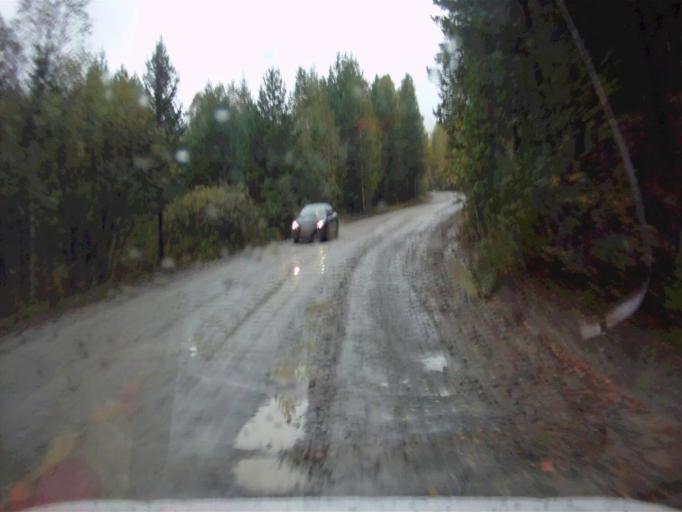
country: RU
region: Chelyabinsk
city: Kyshtym
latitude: 55.7478
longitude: 60.4897
